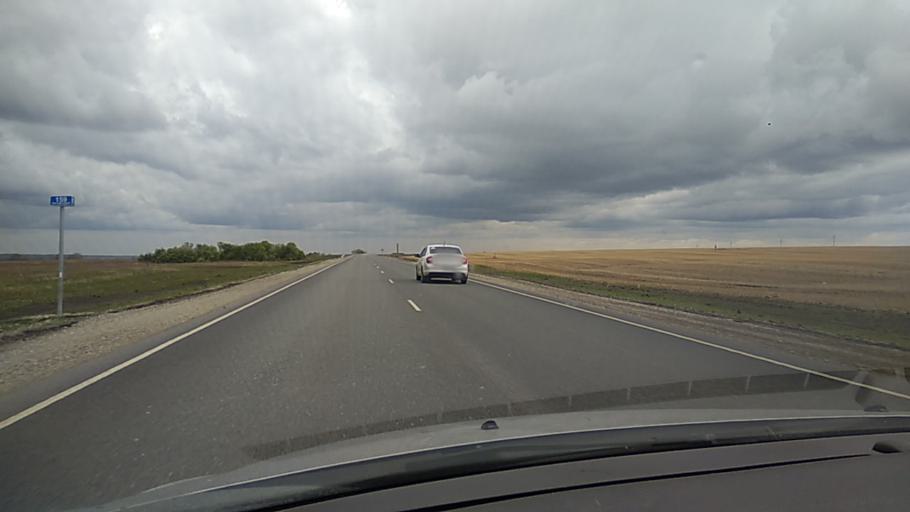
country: RU
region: Kurgan
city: Kataysk
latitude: 56.2881
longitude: 62.7547
